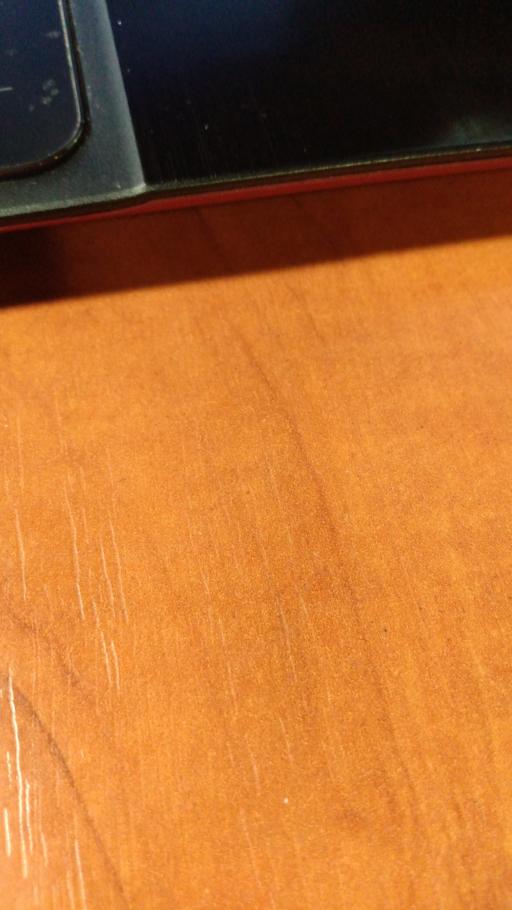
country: RU
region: Republic of Karelia
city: Pudozh
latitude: 62.1265
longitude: 37.5538
